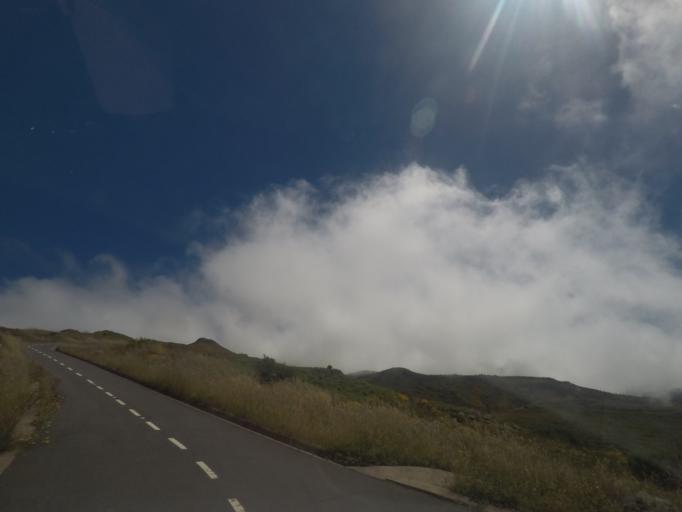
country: PT
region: Madeira
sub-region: Camara de Lobos
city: Curral das Freiras
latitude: 32.7113
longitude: -16.9385
